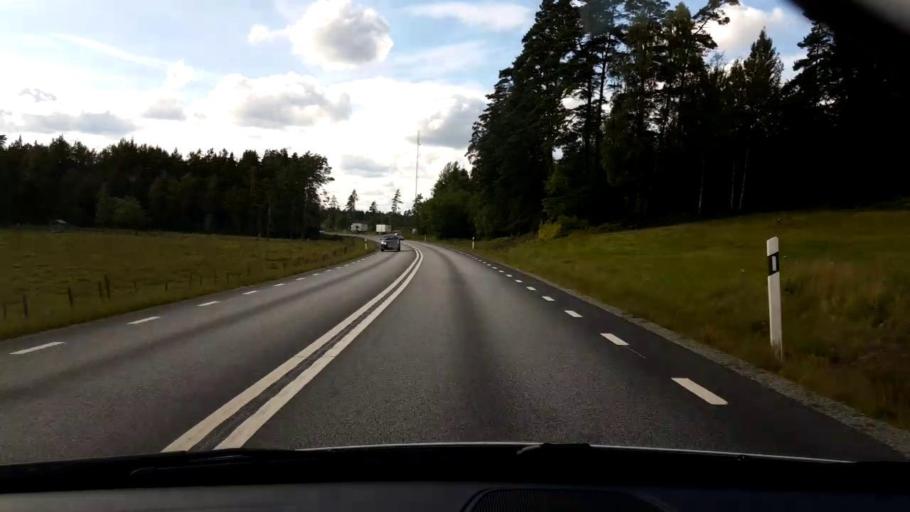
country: SE
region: Joenkoeping
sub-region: Savsjo Kommun
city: Vrigstad
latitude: 57.3646
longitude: 14.4527
